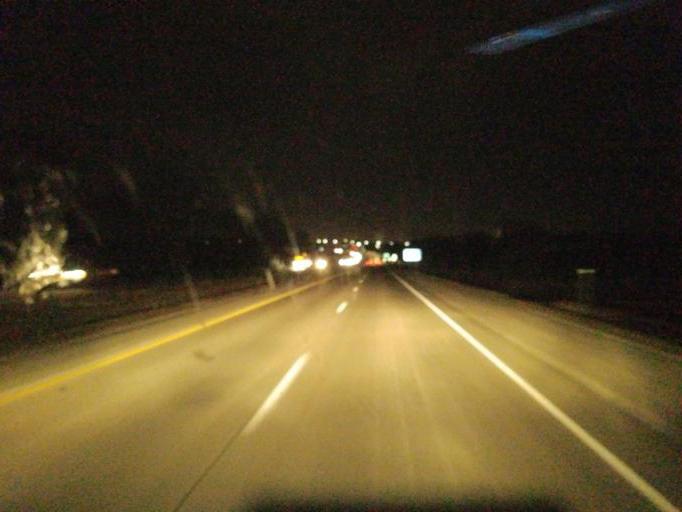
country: US
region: Iowa
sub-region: Dallas County
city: Waukee
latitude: 41.5641
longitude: -93.8718
